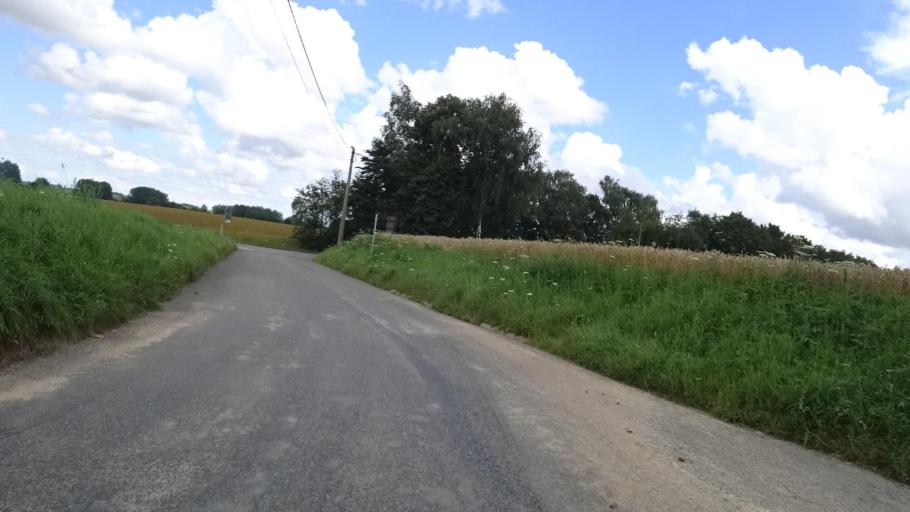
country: BE
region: Wallonia
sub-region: Province du Brabant Wallon
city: Villers-la-Ville
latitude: 50.5508
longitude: 4.5319
